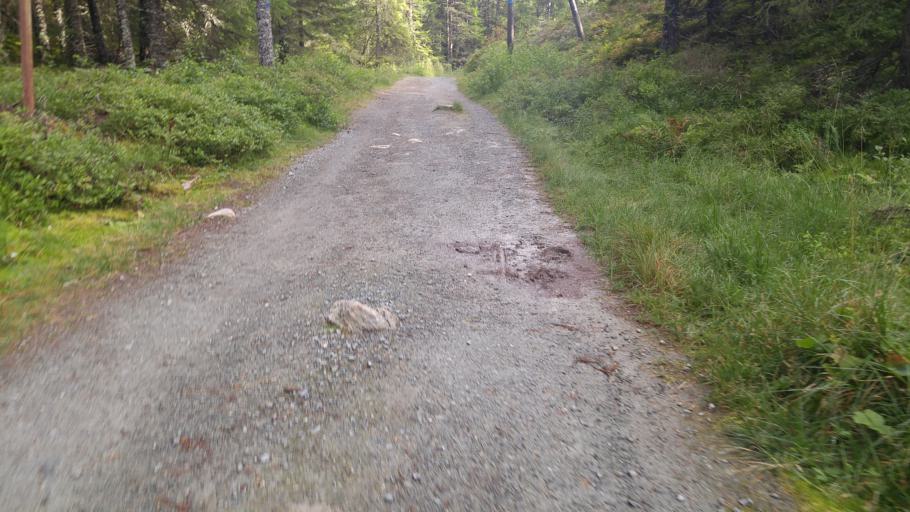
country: NO
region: Sor-Trondelag
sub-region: Trondheim
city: Trondheim
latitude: 63.4132
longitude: 10.3297
